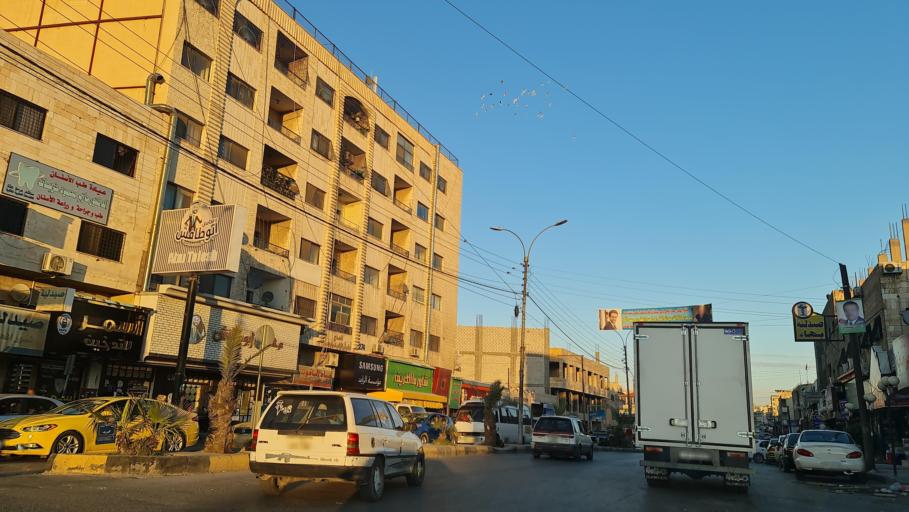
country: JO
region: Zarqa
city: Zarqa
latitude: 32.0781
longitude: 36.0748
